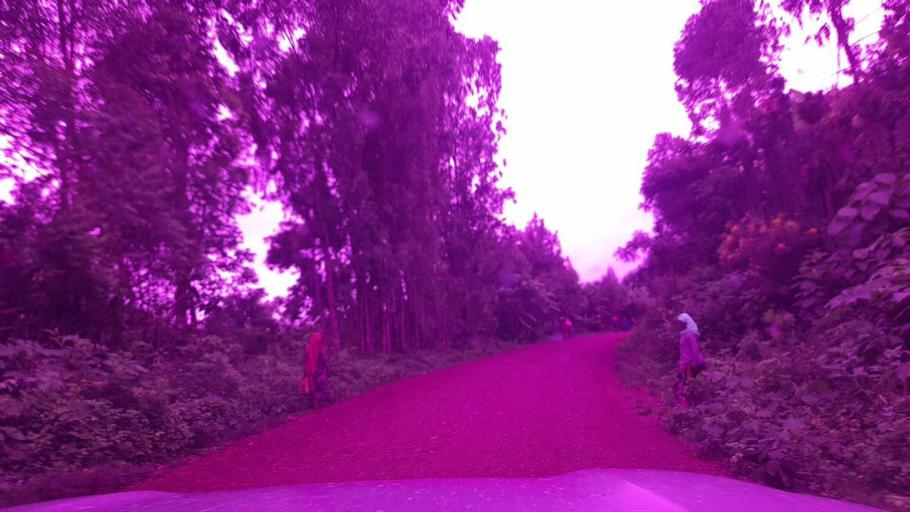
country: ET
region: Southern Nations, Nationalities, and People's Region
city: Bonga
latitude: 7.5855
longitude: 36.0159
